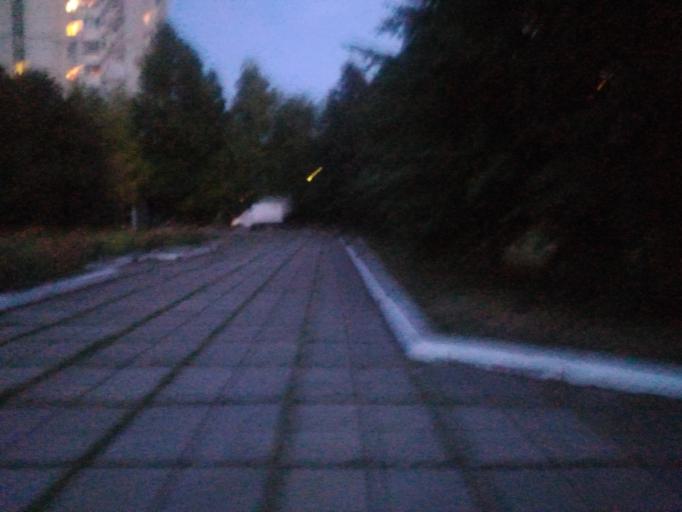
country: RU
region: Ulyanovsk
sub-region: Ulyanovskiy Rayon
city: Ulyanovsk
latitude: 54.3500
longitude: 48.3909
